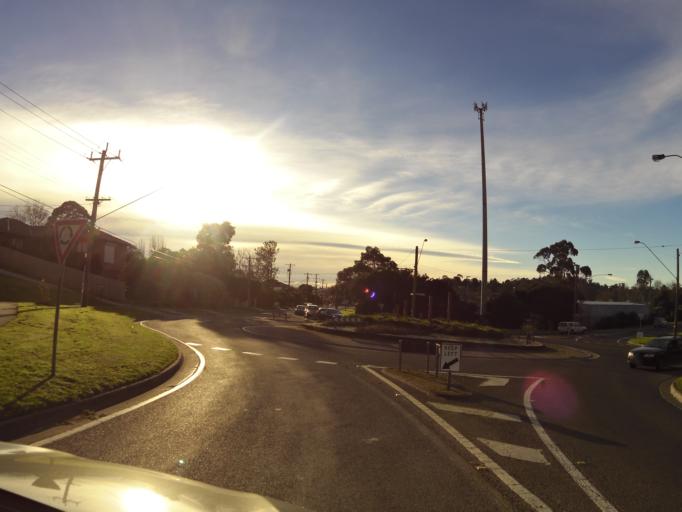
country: AU
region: Victoria
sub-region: Knox
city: Ferntree Gully
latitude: -37.8946
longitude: 145.2927
